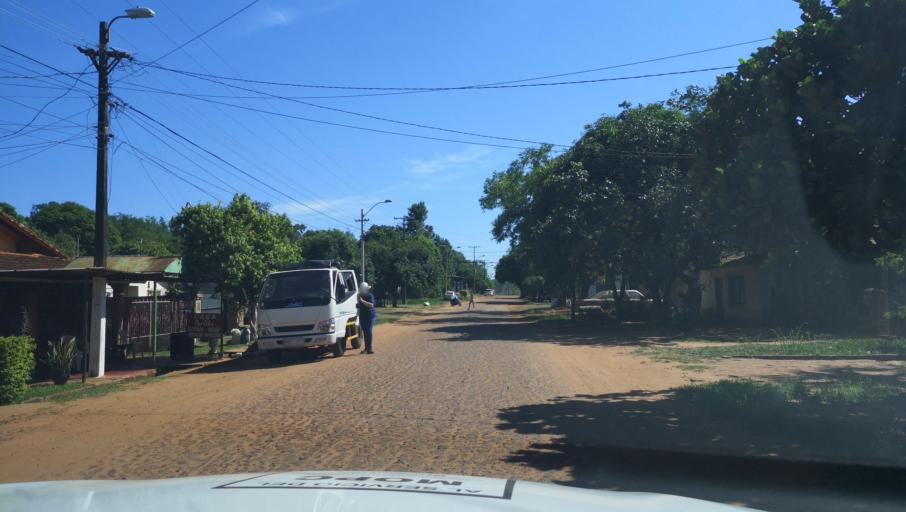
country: PY
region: Misiones
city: Santa Maria
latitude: -26.8824
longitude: -57.0236
